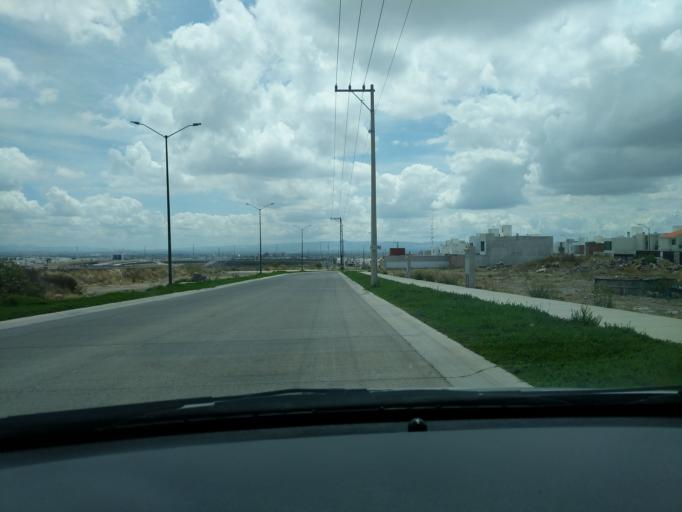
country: MX
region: San Luis Potosi
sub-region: Mexquitic de Carmona
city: Guadalupe Victoria
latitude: 22.1607
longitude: -101.0549
